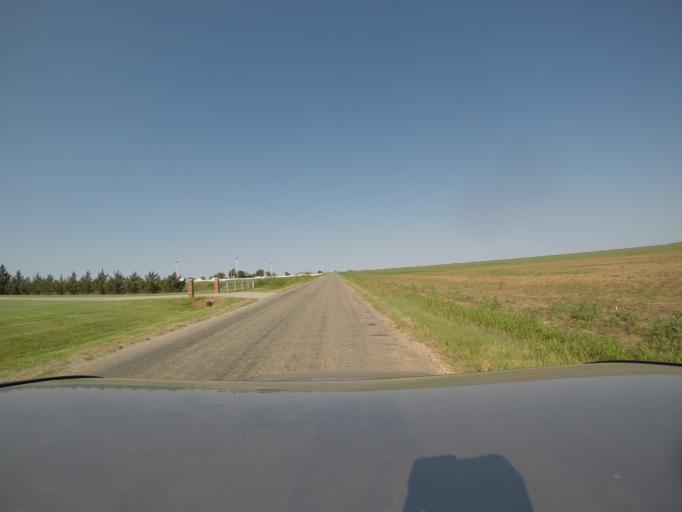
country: US
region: New Mexico
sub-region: Curry County
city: Clovis
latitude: 34.4107
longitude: -103.2159
